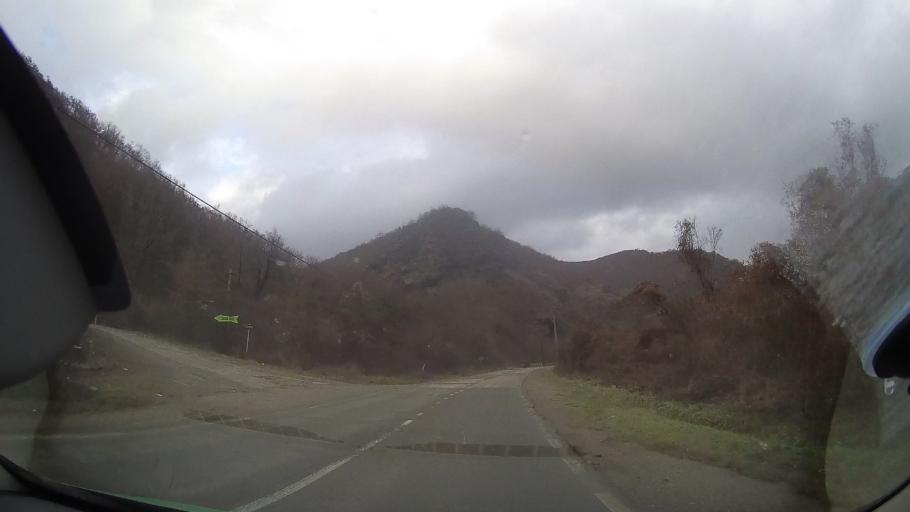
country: RO
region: Cluj
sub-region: Comuna Moldovenesti
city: Moldovenesti
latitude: 46.5066
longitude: 23.6393
